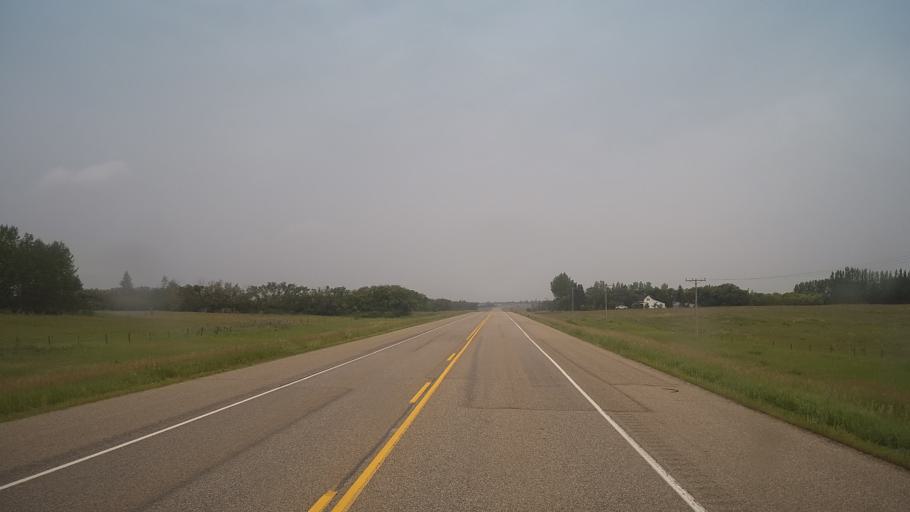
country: CA
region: Saskatchewan
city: Biggar
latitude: 52.0563
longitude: -107.9243
